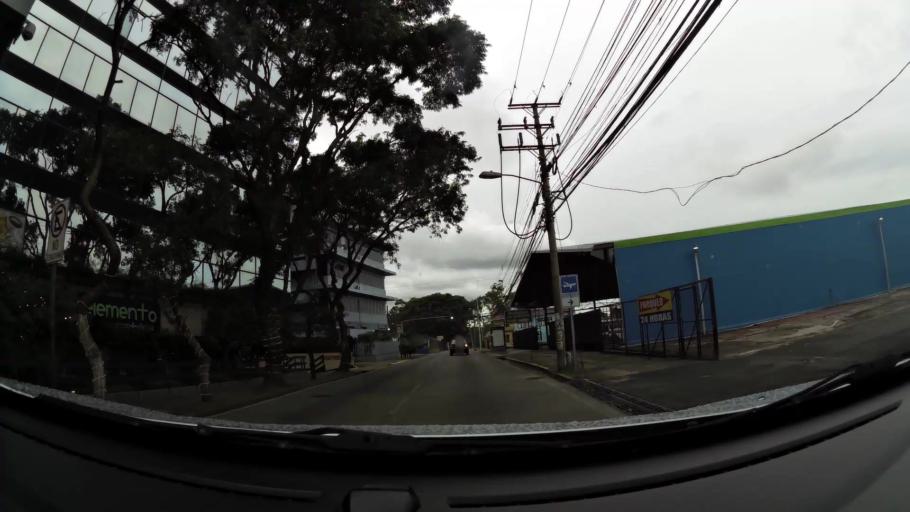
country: CR
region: San Jose
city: San Jose
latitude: 9.9370
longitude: -84.0965
